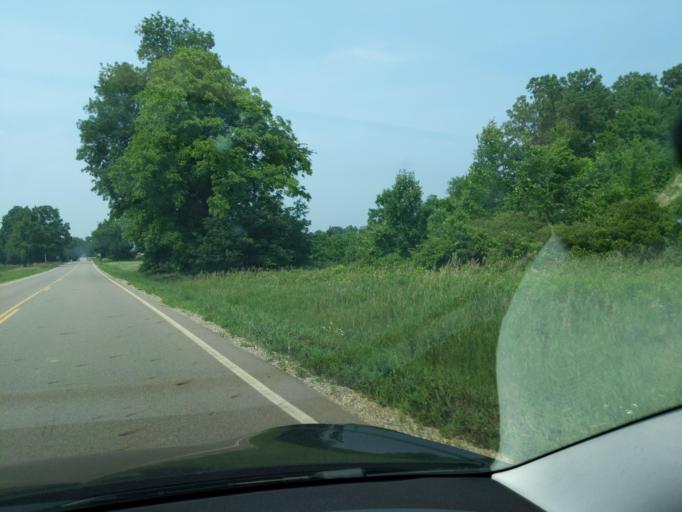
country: US
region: Michigan
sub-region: Clinton County
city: DeWitt
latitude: 42.8678
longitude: -84.5723
